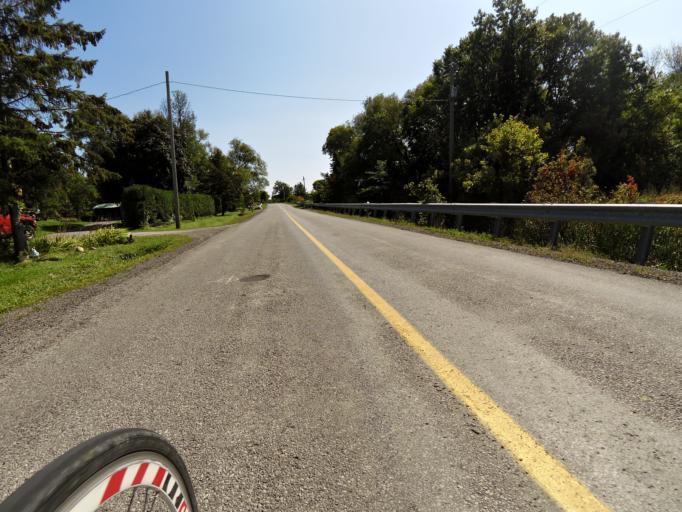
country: CA
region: Ontario
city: Bells Corners
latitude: 45.4399
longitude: -76.0702
